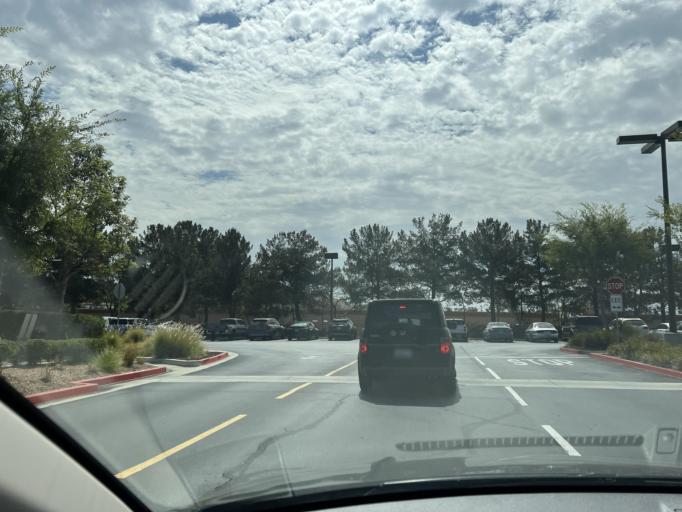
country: US
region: California
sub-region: San Diego County
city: Escondido
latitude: 33.1362
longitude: -117.1247
